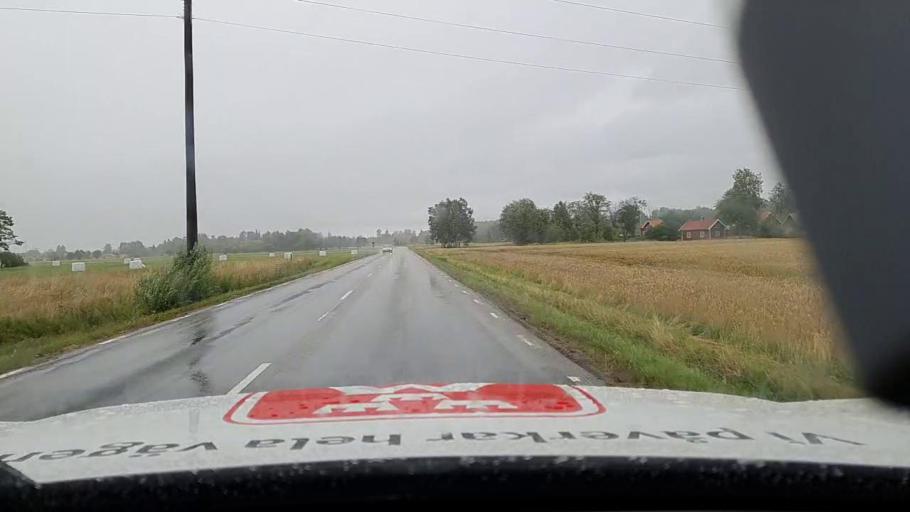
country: SE
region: Vaestra Goetaland
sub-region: Toreboda Kommun
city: Toereboda
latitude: 58.6937
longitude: 14.1305
